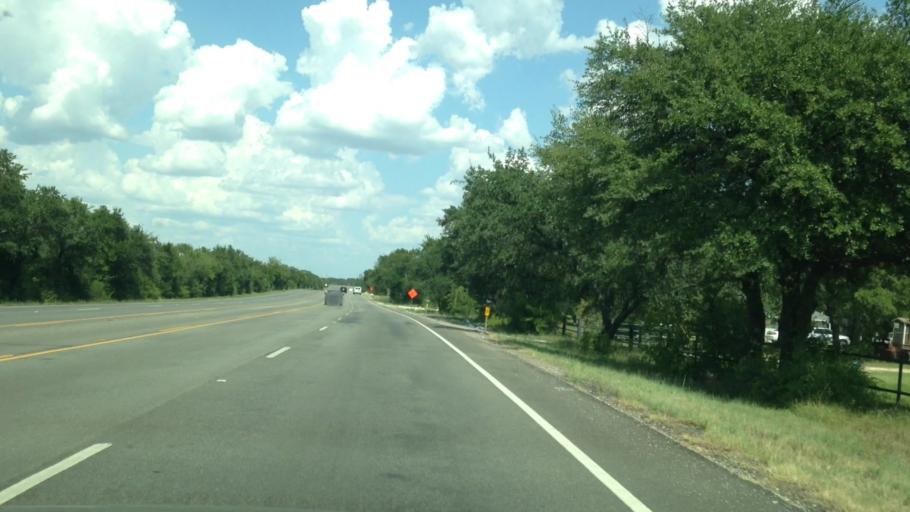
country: US
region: Texas
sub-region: Williamson County
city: Georgetown
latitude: 30.6314
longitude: -97.7412
